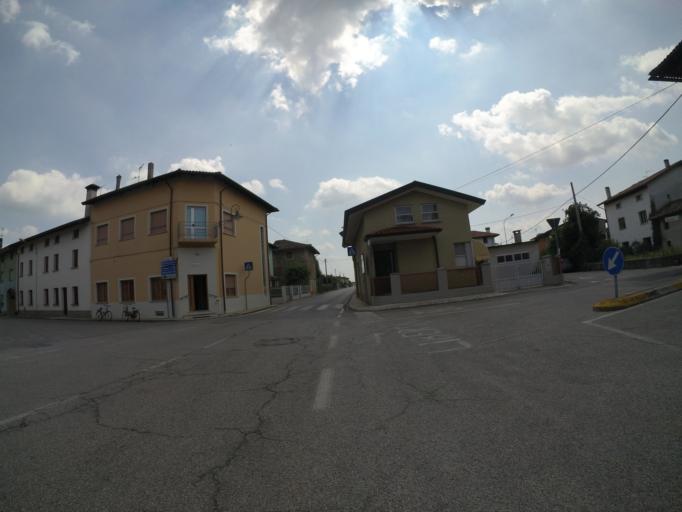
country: IT
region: Friuli Venezia Giulia
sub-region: Provincia di Udine
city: Basiliano
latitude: 46.0114
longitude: 13.0701
